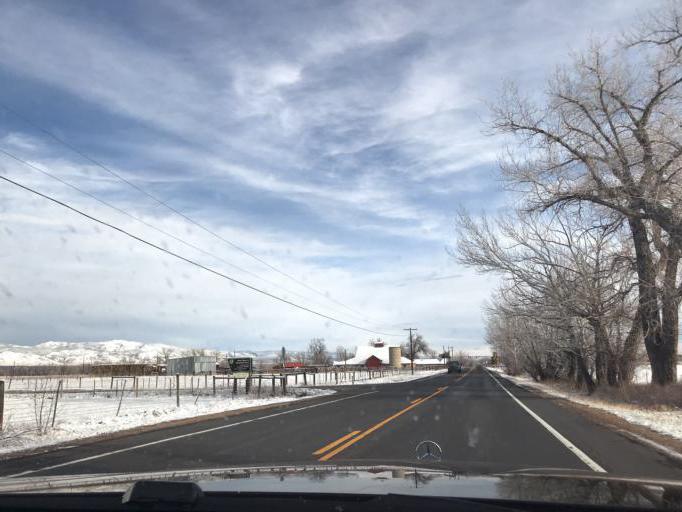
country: US
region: Colorado
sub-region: Boulder County
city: Superior
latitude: 39.9829
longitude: -105.2128
